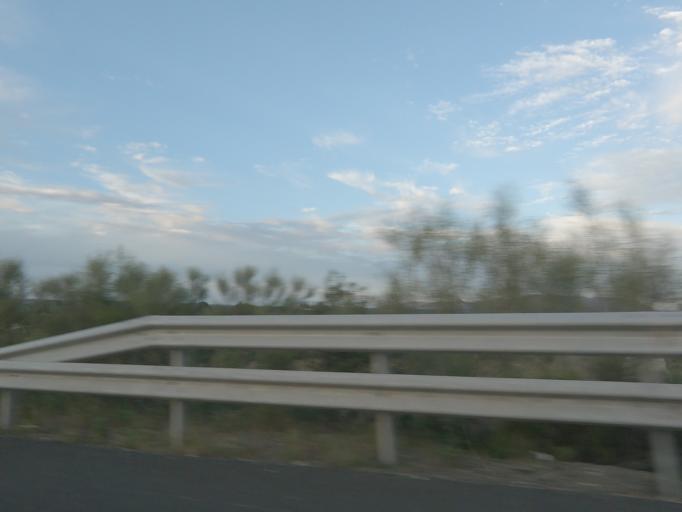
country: ES
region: Extremadura
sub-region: Provincia de Caceres
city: Alcuescar
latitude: 39.1824
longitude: -6.2748
